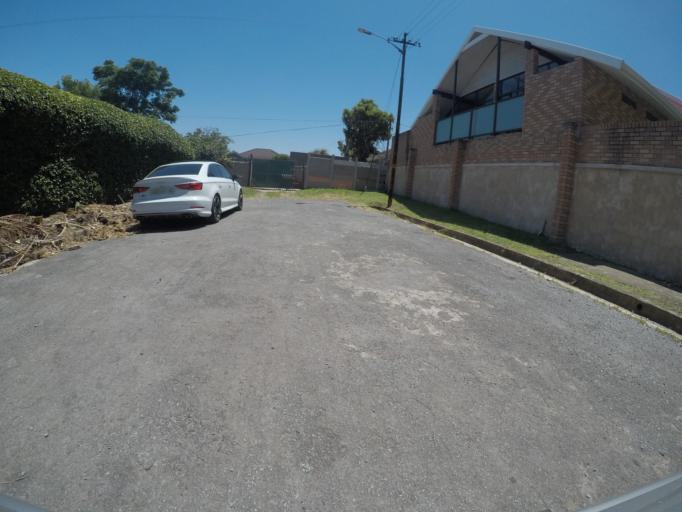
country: ZA
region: Eastern Cape
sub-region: Buffalo City Metropolitan Municipality
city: East London
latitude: -32.9904
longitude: 27.9079
